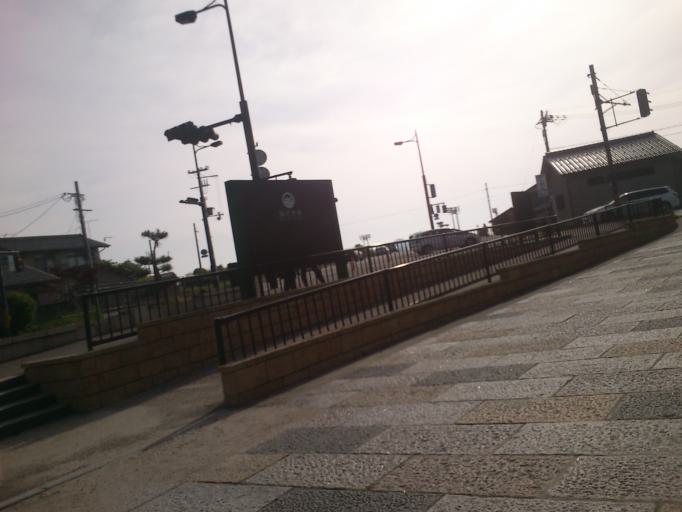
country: JP
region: Kyoto
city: Miyazu
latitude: 35.5813
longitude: 135.1962
